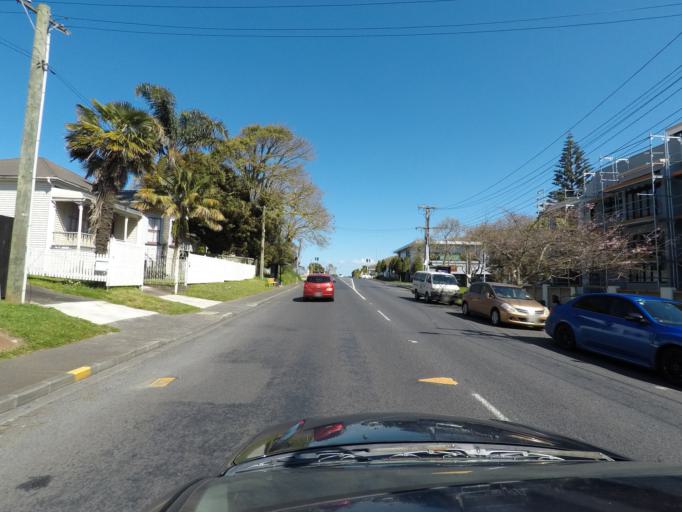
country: NZ
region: Auckland
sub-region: Auckland
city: Tamaki
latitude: -36.9275
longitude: 174.8437
